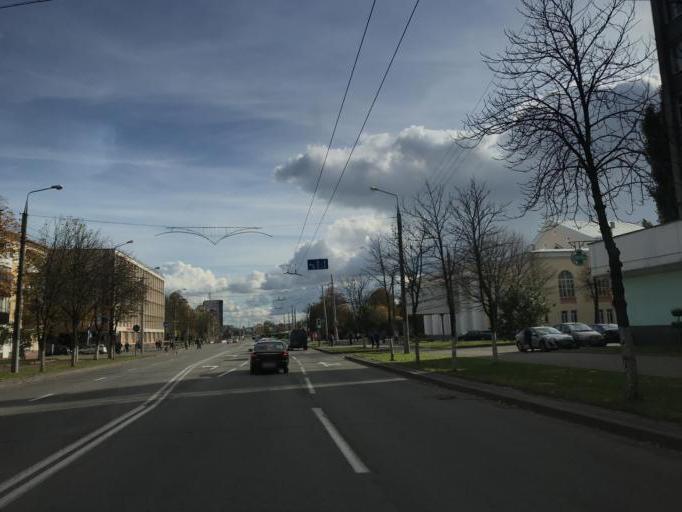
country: BY
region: Gomel
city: Gomel
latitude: 52.4493
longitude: 30.9679
